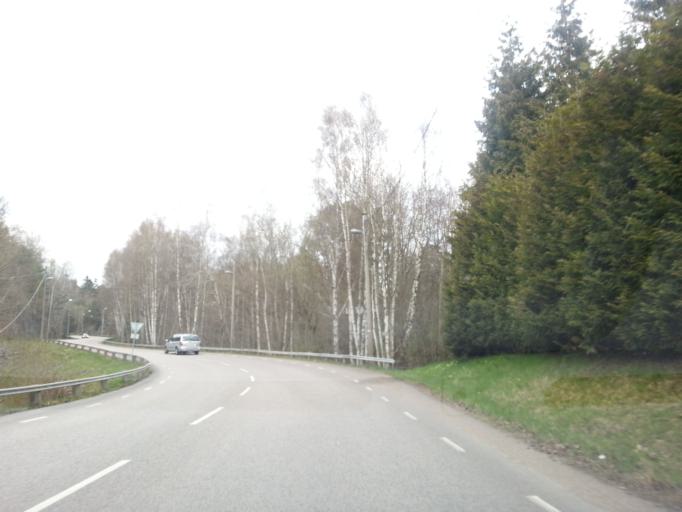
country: SE
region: Vaestra Goetaland
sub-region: Goteborg
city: Hammarkullen
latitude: 57.7909
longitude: 12.0315
